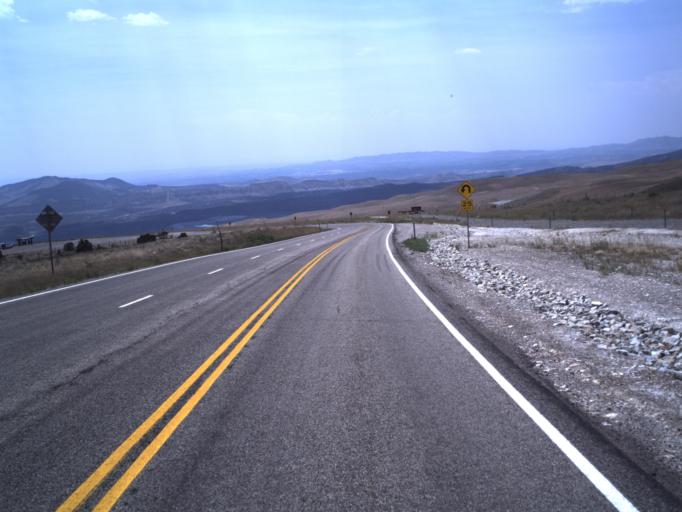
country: US
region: Utah
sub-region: Uintah County
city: Vernal
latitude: 40.6437
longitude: -109.4876
